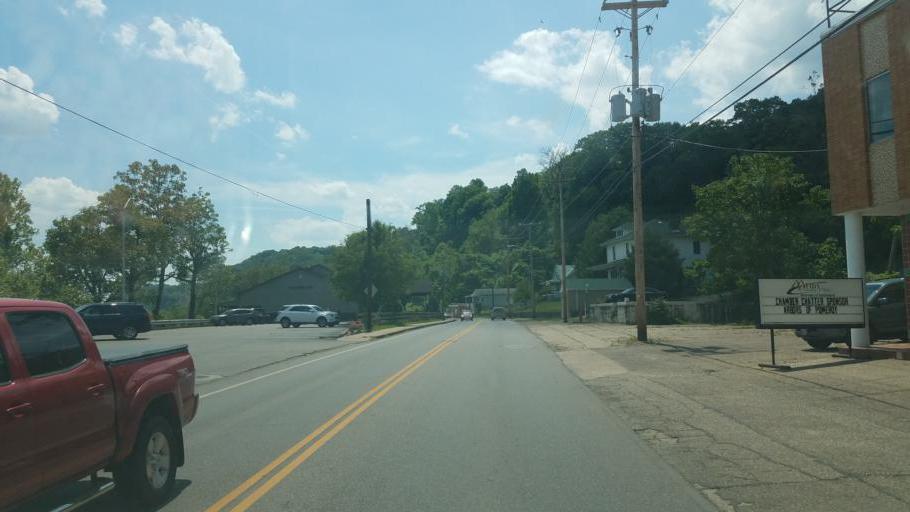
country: US
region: Ohio
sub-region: Meigs County
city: Pomeroy
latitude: 39.0250
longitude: -82.0378
